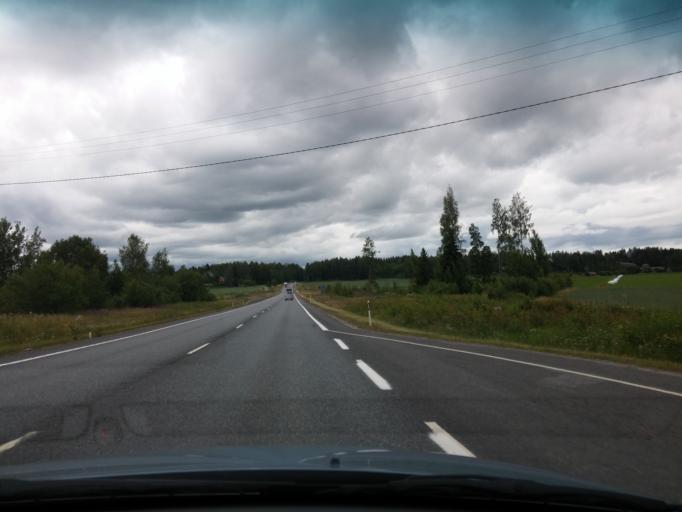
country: FI
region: Uusimaa
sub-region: Porvoo
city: Porvoo
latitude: 60.4125
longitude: 25.5818
